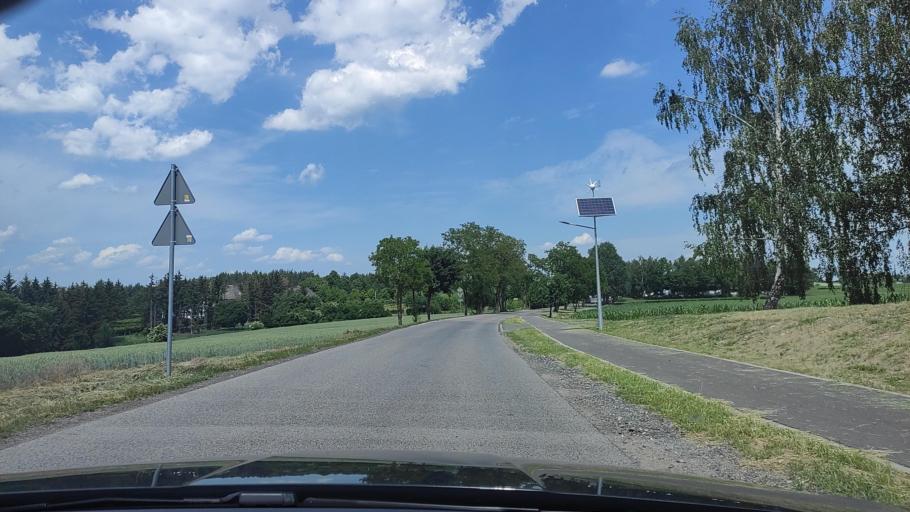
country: PL
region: Greater Poland Voivodeship
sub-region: Powiat gnieznienski
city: Lubowo
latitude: 52.5095
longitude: 17.3826
